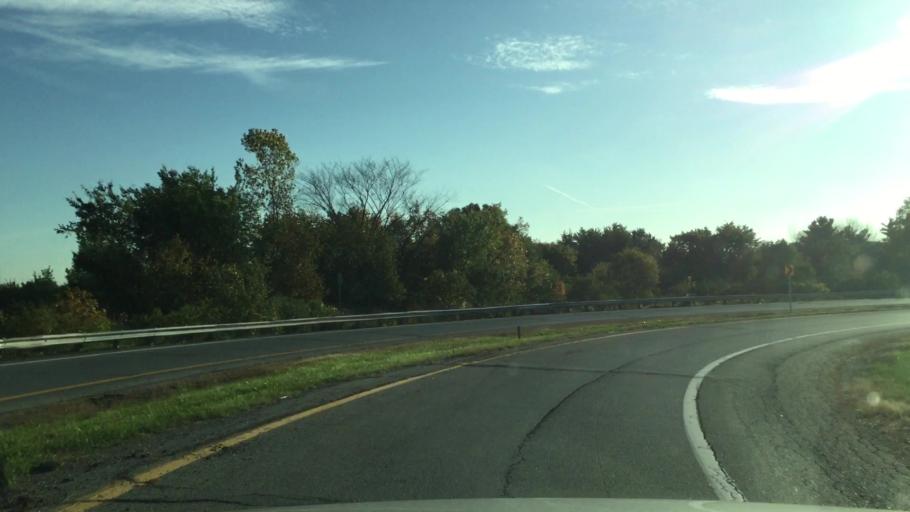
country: US
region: Michigan
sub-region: Oakland County
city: Troy
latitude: 42.5999
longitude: -83.1613
